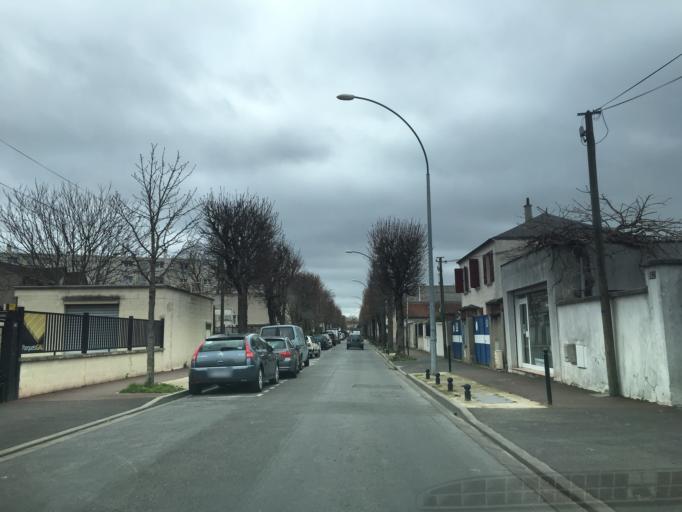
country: FR
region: Ile-de-France
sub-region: Departement du Val-de-Marne
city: Saint-Maur-des-Fosses
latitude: 48.7908
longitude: 2.4913
